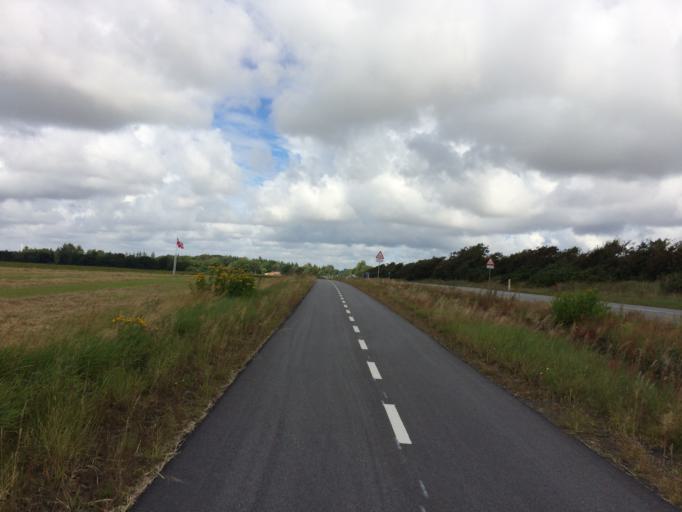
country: DK
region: Central Jutland
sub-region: Holstebro Kommune
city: Ulfborg
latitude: 56.3259
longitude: 8.3429
